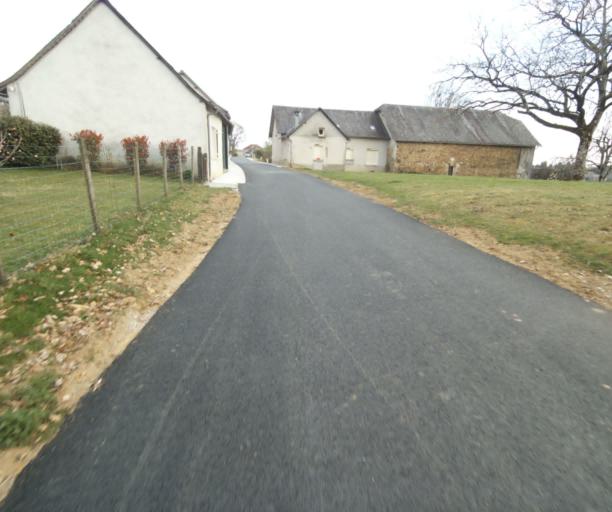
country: FR
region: Limousin
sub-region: Departement de la Correze
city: Saint-Clement
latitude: 45.3590
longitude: 1.6369
